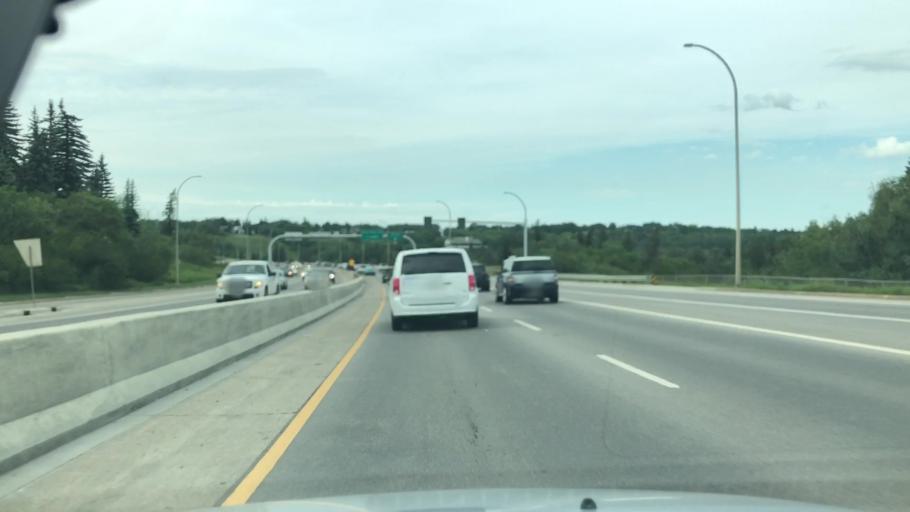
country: CA
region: Alberta
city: Edmonton
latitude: 53.5526
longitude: -113.4375
